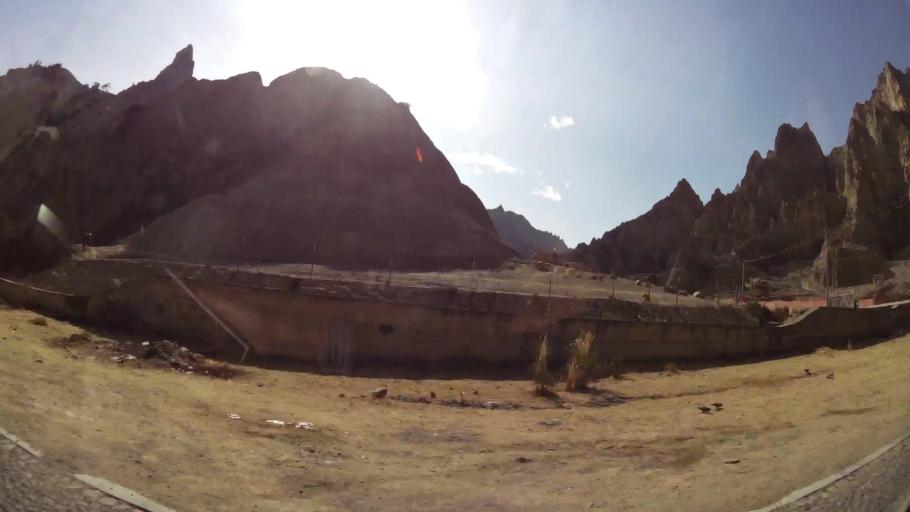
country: BO
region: La Paz
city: La Paz
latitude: -16.5131
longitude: -68.0626
